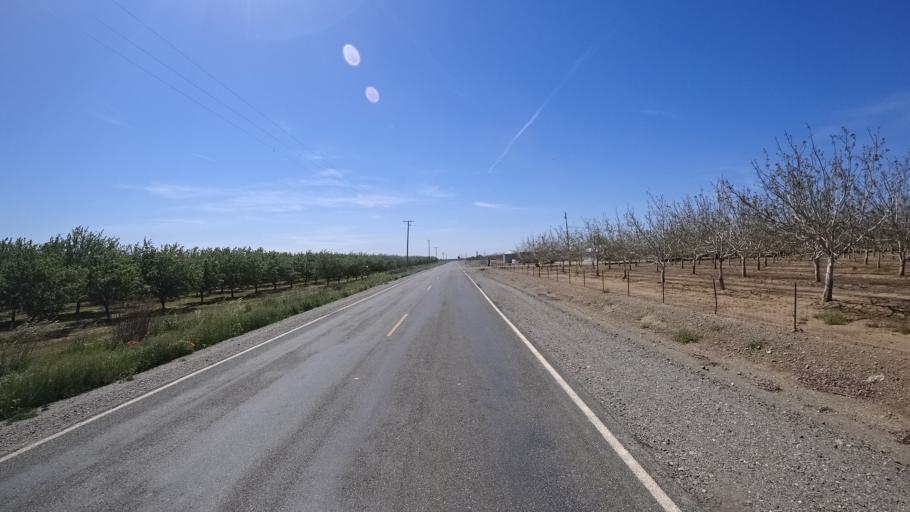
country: US
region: California
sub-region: Glenn County
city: Orland
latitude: 39.7006
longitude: -122.1405
